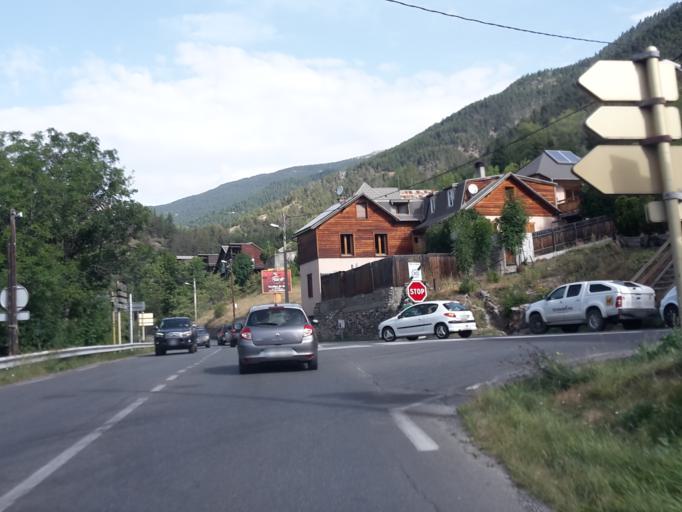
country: FR
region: Provence-Alpes-Cote d'Azur
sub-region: Departement des Hautes-Alpes
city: Saint-Chaffrey
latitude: 44.9163
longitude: 6.6225
